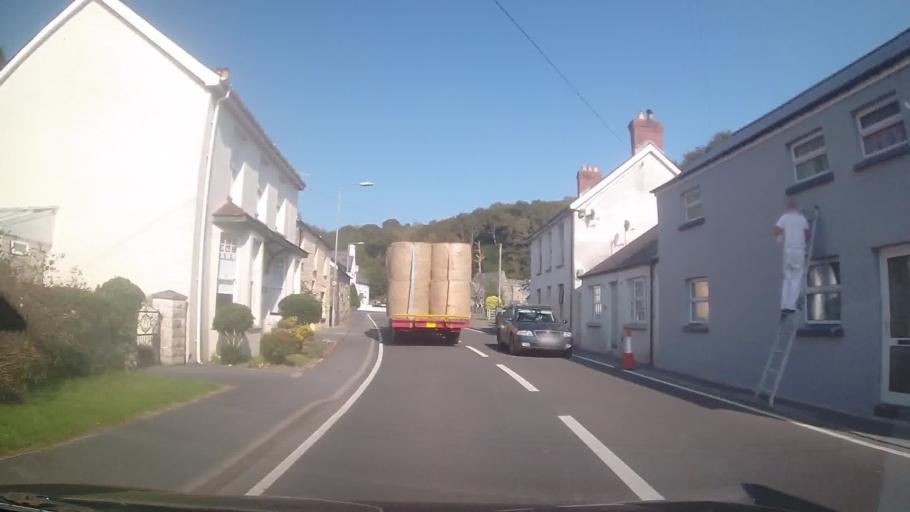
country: GB
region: Wales
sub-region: Pembrokeshire
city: Nevern
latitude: 52.0166
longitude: -4.7693
